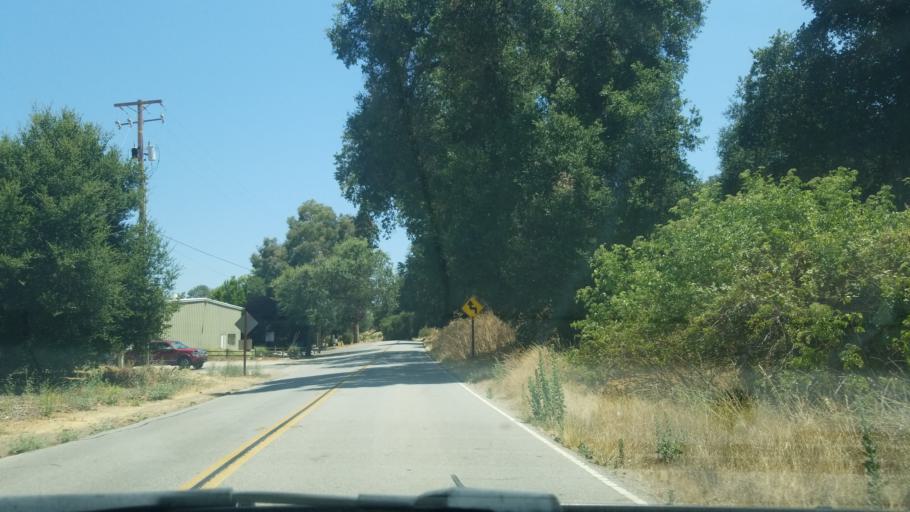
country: US
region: California
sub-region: San Luis Obispo County
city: Atascadero
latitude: 35.4971
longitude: -120.6535
